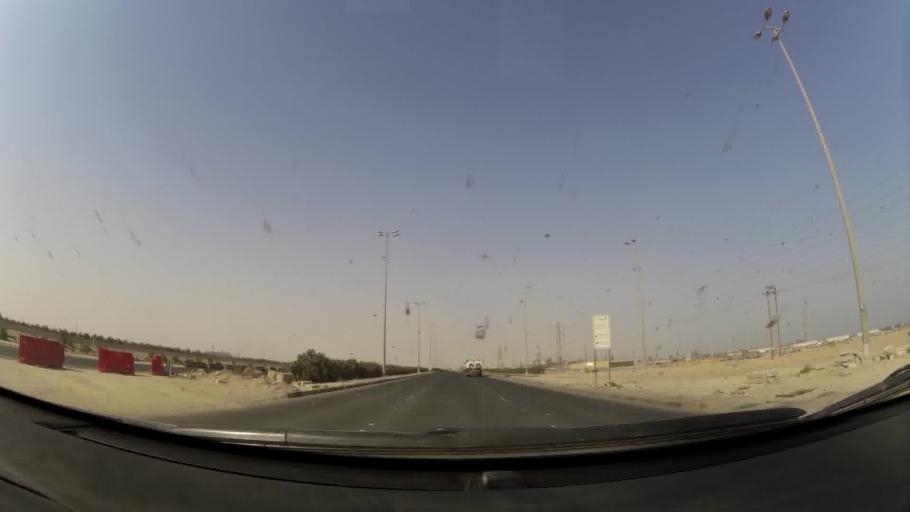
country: KW
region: Al Ahmadi
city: Al Fahahil
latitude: 28.9764
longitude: 48.1586
